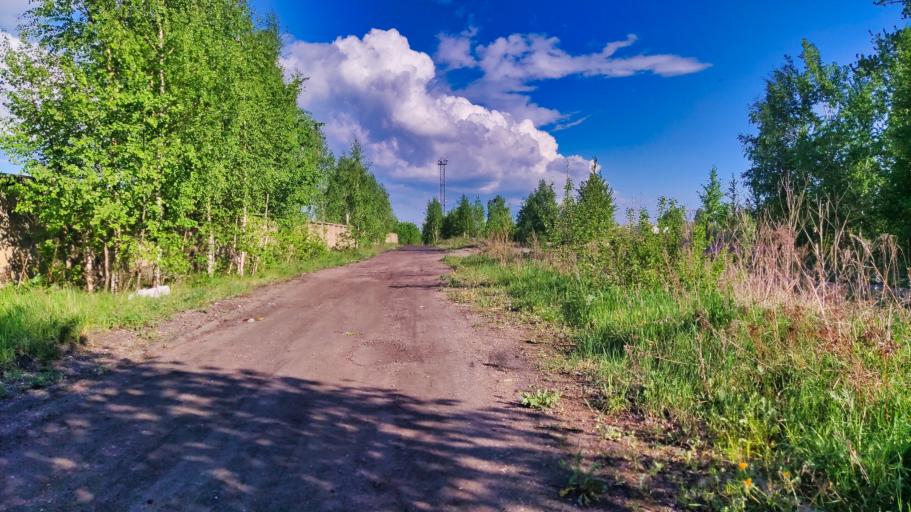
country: RU
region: Tverskaya
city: Rzhev
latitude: 56.2408
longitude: 34.3400
